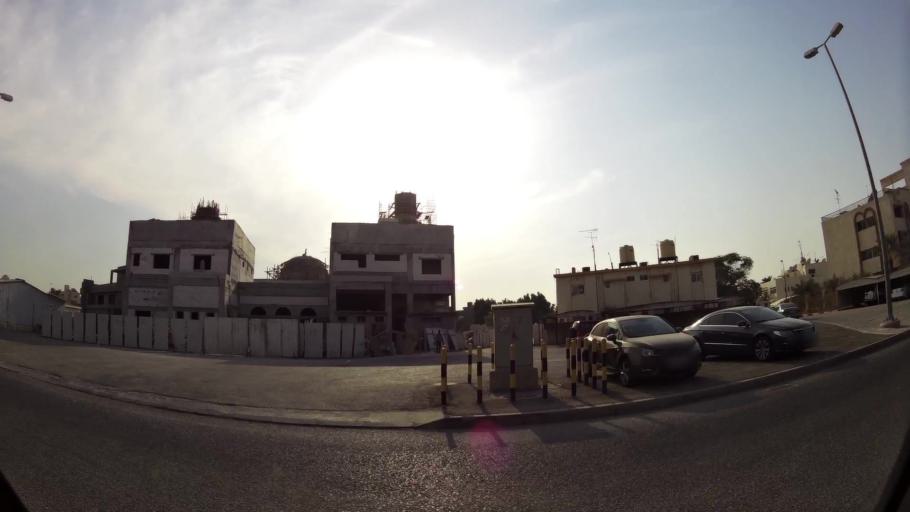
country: KW
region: Muhafazat Hawalli
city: Hawalli
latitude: 29.3250
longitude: 48.0081
